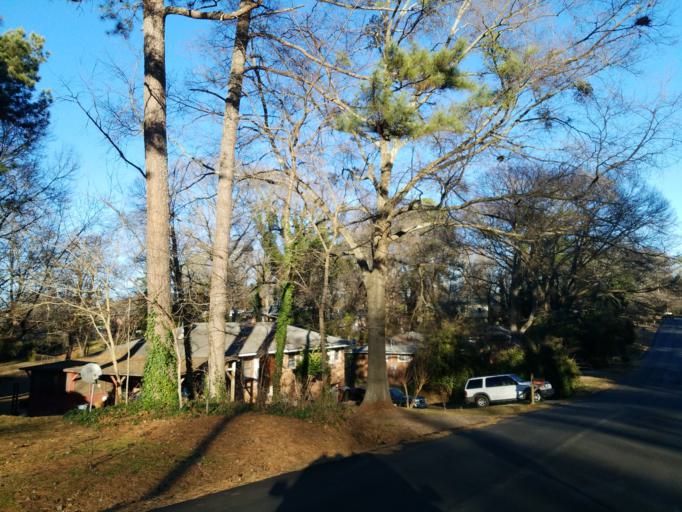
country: US
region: Georgia
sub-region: Cobb County
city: Fair Oaks
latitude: 33.9406
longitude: -84.4954
